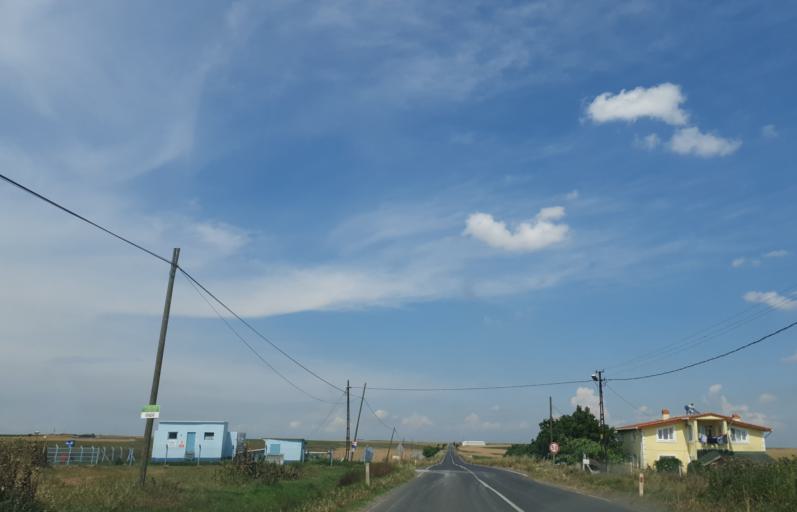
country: TR
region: Kirklareli
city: Buyukkaristiran
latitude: 41.2348
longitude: 27.5865
